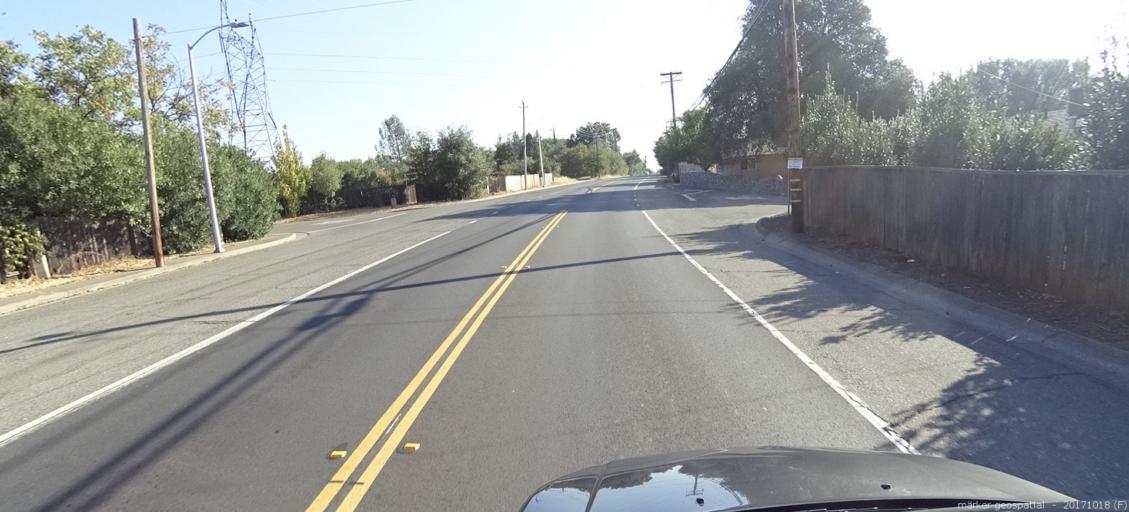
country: US
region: California
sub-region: Shasta County
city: Redding
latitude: 40.5346
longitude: -122.3330
